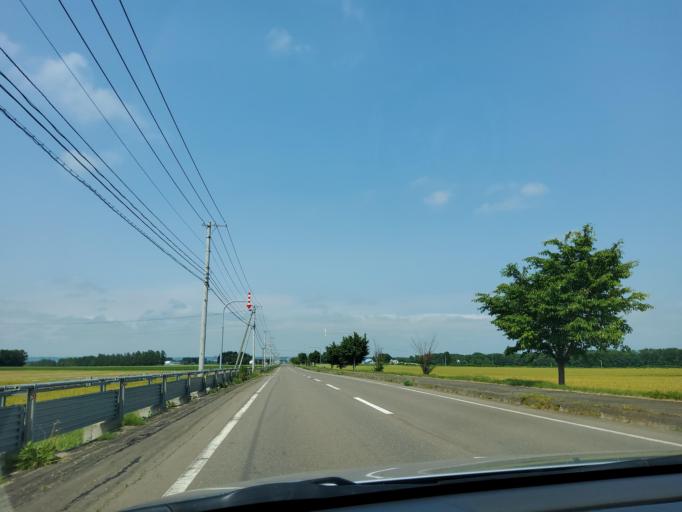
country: JP
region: Hokkaido
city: Obihiro
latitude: 42.8836
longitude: 143.0342
